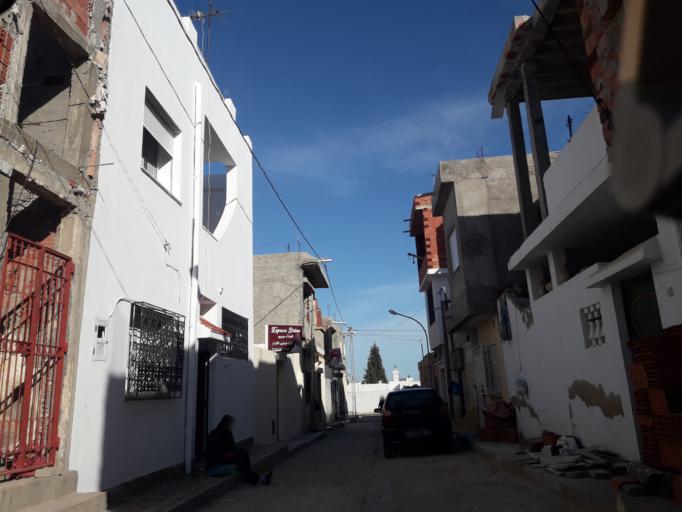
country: TN
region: Safaqis
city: Sfax
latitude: 34.7419
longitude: 10.5263
